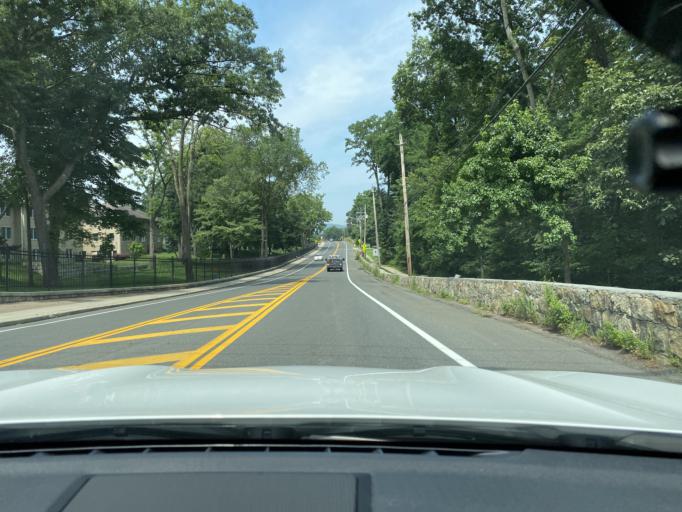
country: US
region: New York
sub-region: Rockland County
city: Suffern
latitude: 41.1128
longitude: -74.1381
